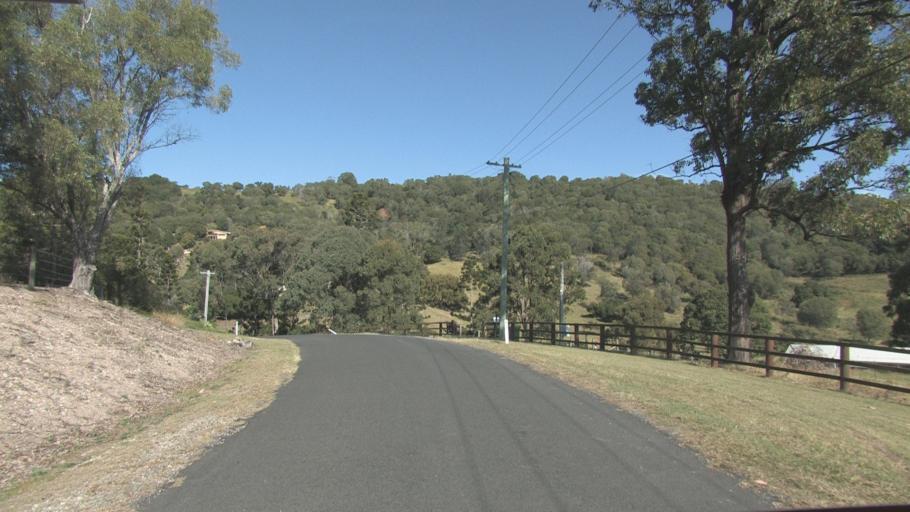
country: AU
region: Queensland
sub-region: Logan
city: Windaroo
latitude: -27.7428
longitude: 153.1721
